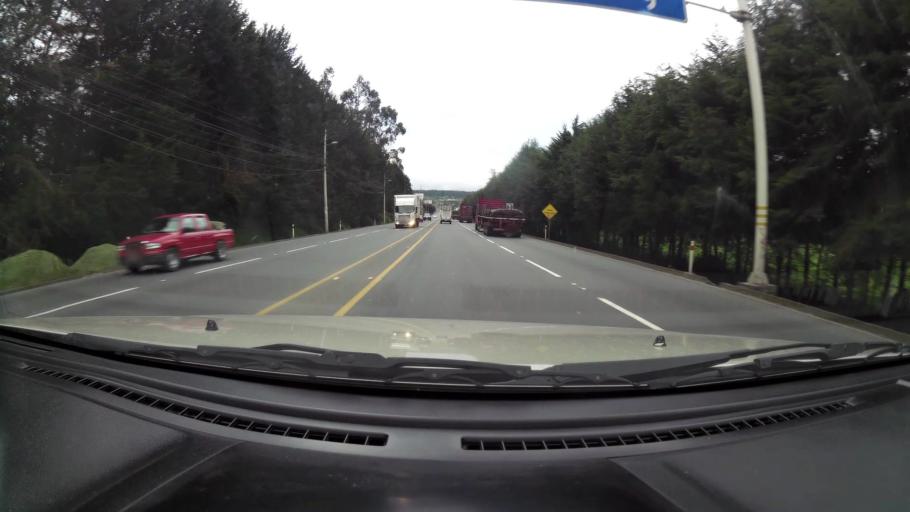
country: EC
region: Pichincha
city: Machachi
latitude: -0.4530
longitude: -78.5916
